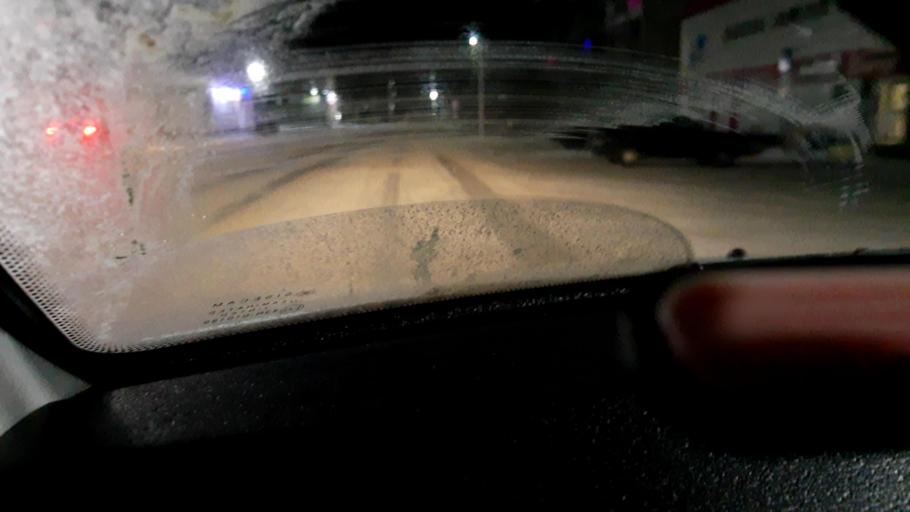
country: RU
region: Nizjnij Novgorod
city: Bogorodsk
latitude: 56.1001
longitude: 43.4737
